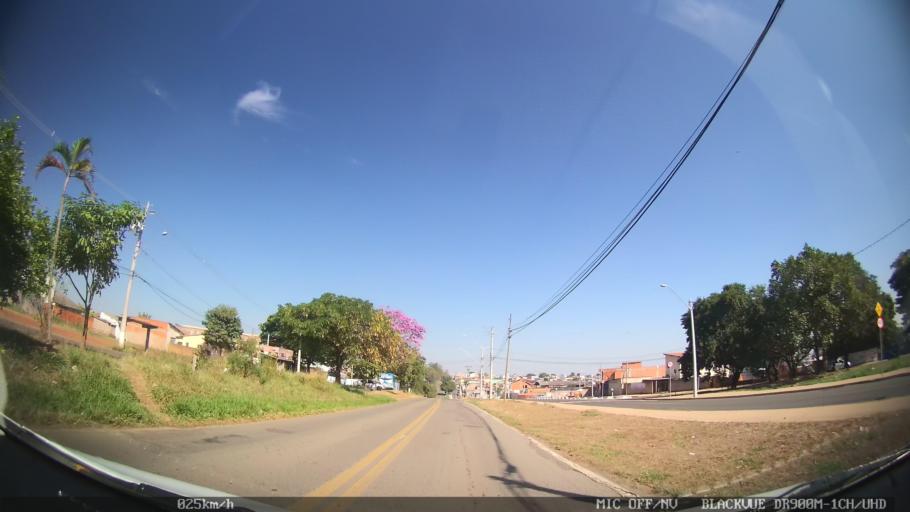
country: BR
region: Sao Paulo
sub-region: Indaiatuba
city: Indaiatuba
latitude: -23.0346
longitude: -47.1059
